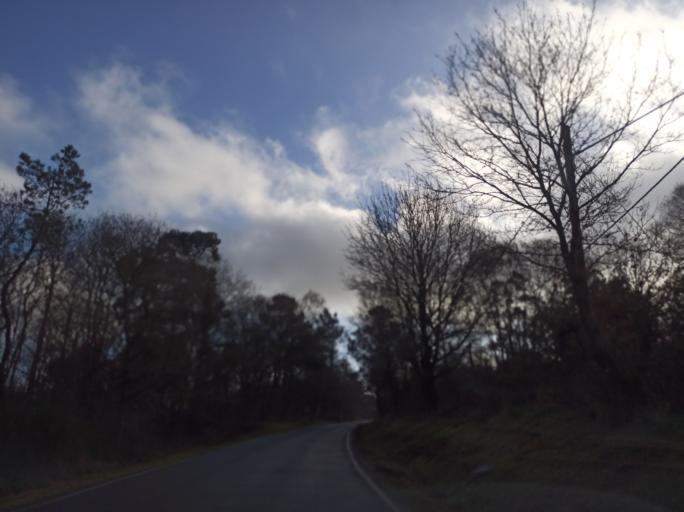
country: ES
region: Galicia
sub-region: Provincia da Coruna
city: Curtis
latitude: 43.0980
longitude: -7.9846
